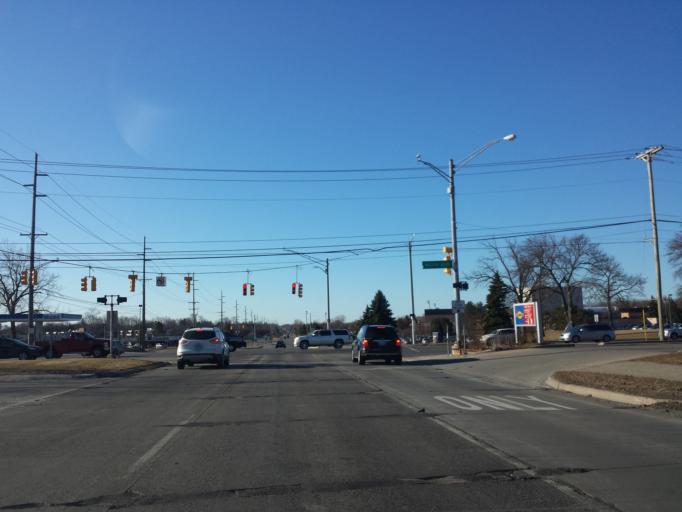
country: US
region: Michigan
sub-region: Oakland County
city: Rochester
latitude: 42.6822
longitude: -83.1536
